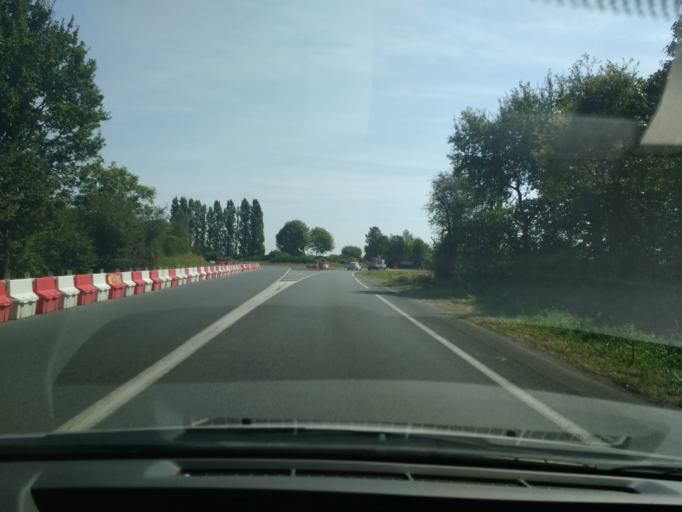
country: FR
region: Pays de la Loire
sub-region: Departement de Maine-et-Loire
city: Andard
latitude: 47.4651
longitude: -0.4101
